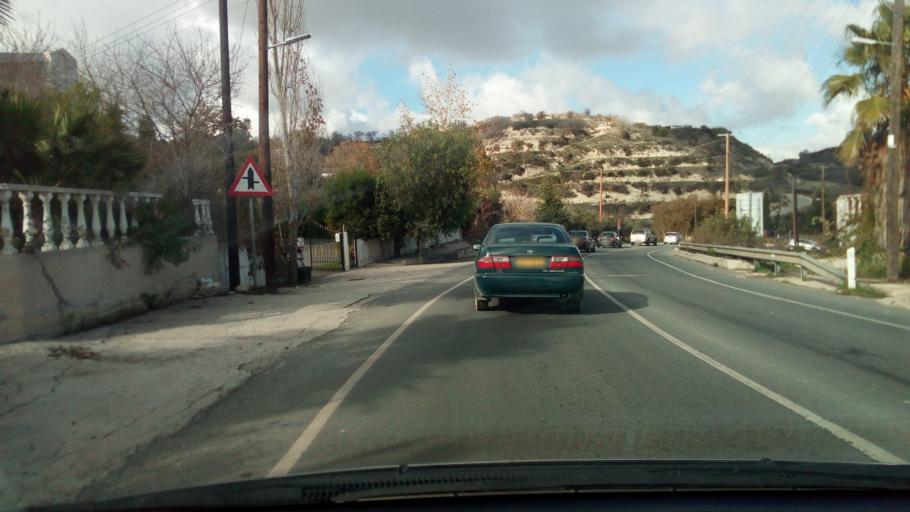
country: CY
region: Pafos
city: Mesogi
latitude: 34.8432
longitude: 32.4669
